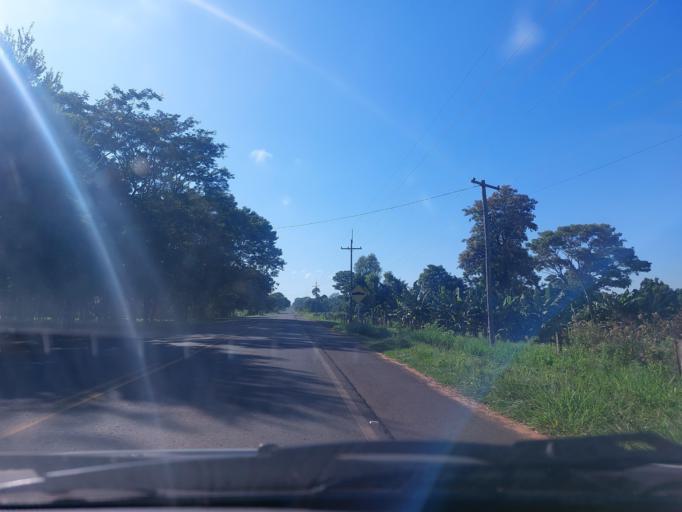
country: PY
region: San Pedro
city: Guayaybi
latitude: -24.5318
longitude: -56.4813
